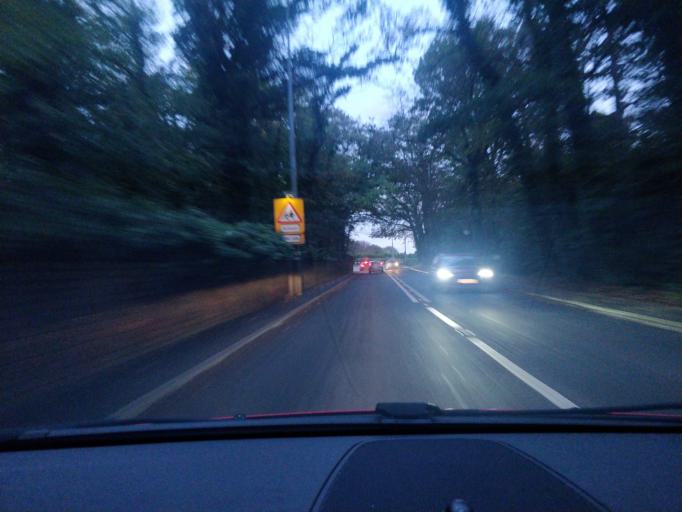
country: GB
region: England
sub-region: Lancashire
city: Ormskirk
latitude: 53.6065
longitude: -2.9334
